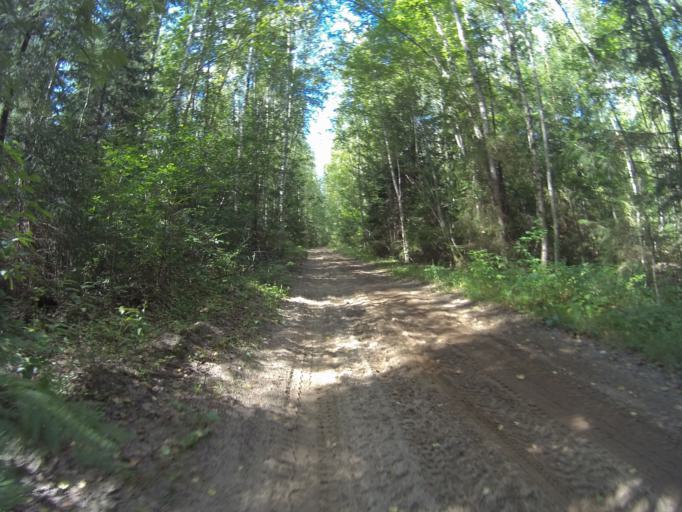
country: RU
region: Vladimir
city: Raduzhnyy
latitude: 55.9041
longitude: 40.2024
